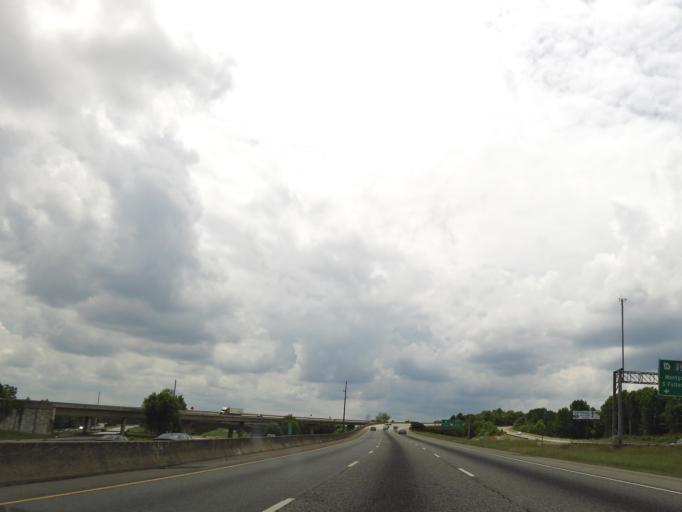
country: US
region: Georgia
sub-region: Fulton County
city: College Park
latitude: 33.6204
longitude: -84.4807
